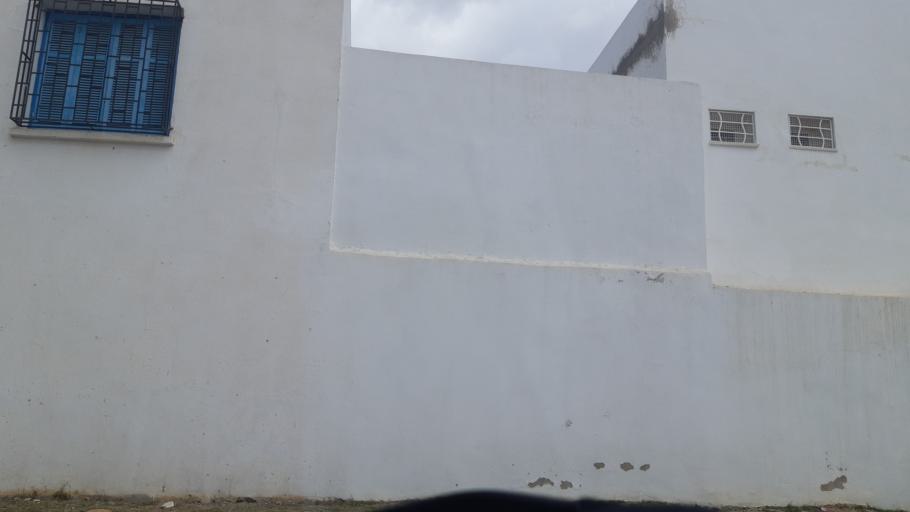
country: TN
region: Susah
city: Akouda
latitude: 35.8620
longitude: 10.5412
